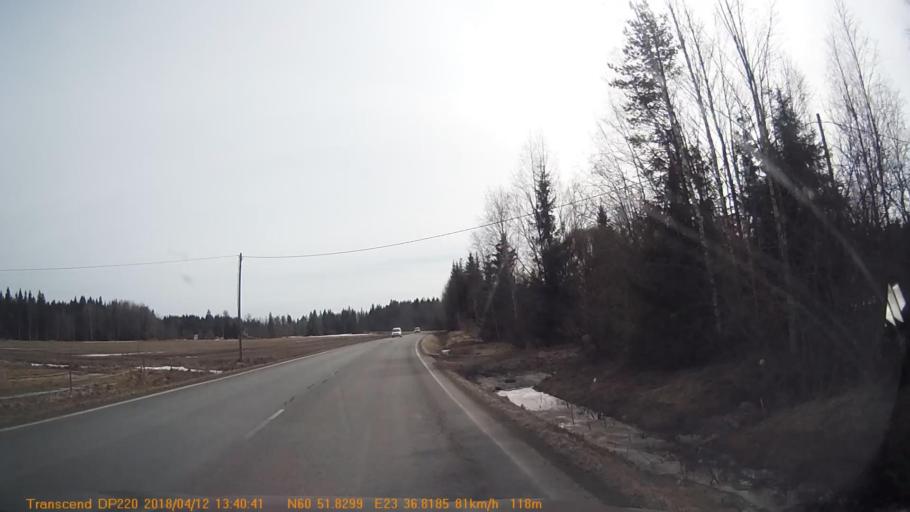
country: FI
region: Haeme
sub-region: Forssa
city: Forssa
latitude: 60.8631
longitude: 23.6140
